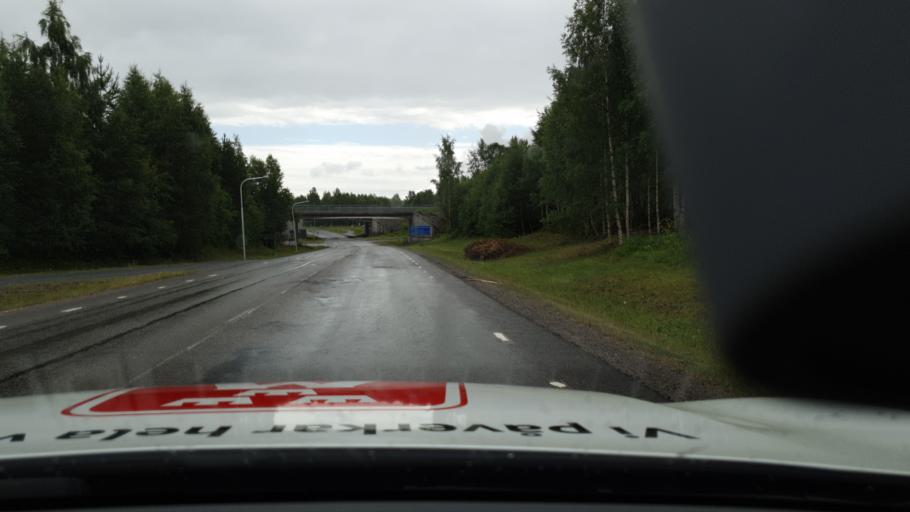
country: SE
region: Norrbotten
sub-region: Lulea Kommun
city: Sodra Sunderbyn
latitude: 65.5505
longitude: 21.8447
